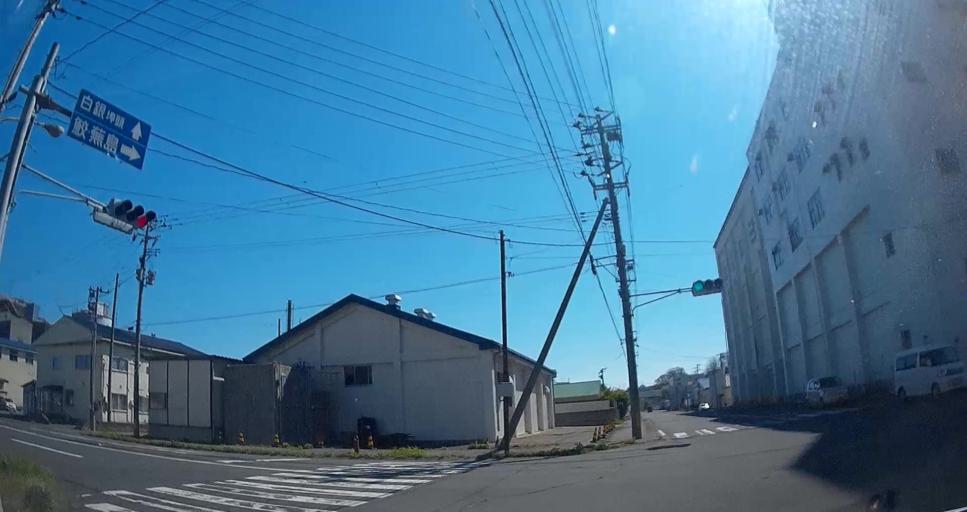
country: JP
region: Aomori
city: Hachinohe
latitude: 40.5271
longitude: 141.5447
